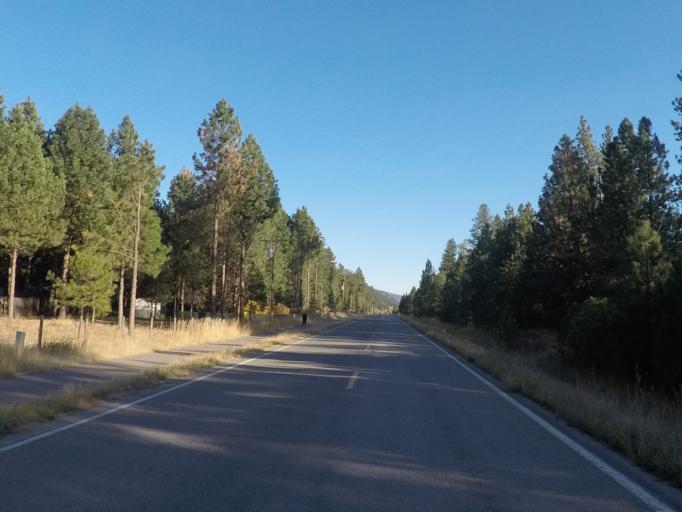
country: US
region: Montana
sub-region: Missoula County
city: Bonner-West Riverside
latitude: 46.8406
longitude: -113.8348
